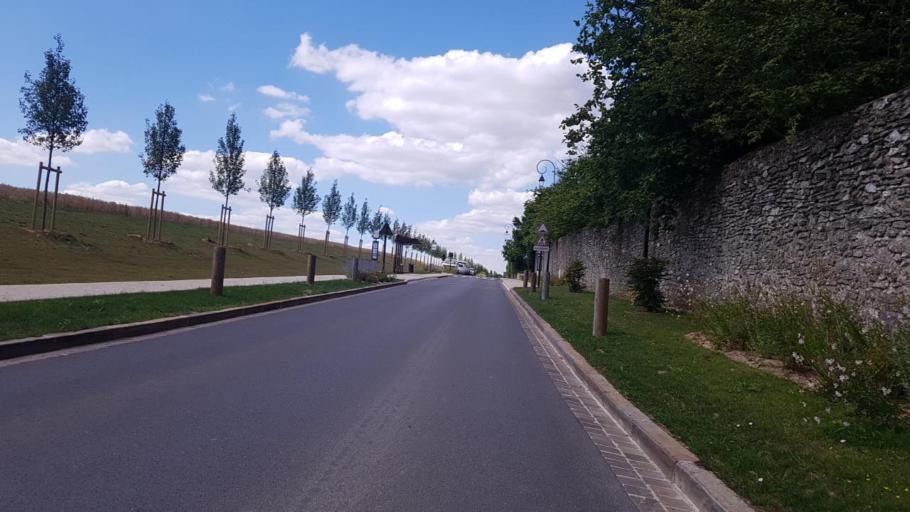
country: FR
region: Ile-de-France
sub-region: Departement de Seine-et-Marne
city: Longperrier
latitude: 49.0204
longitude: 2.6477
